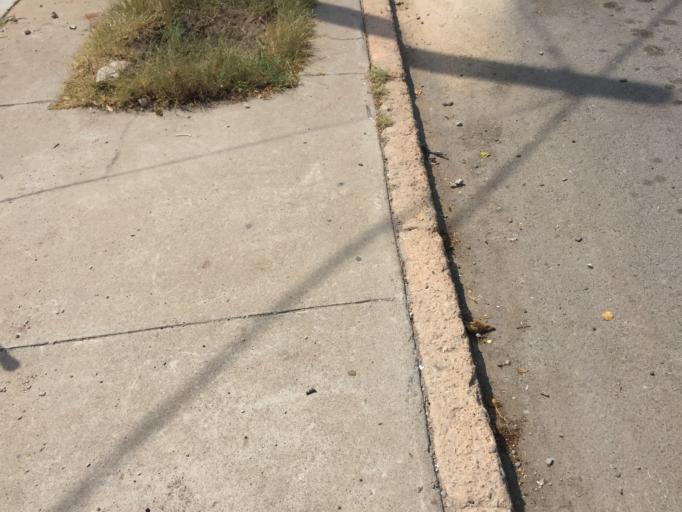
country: MX
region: Sonora
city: Hermosillo
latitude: 29.1039
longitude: -110.9652
